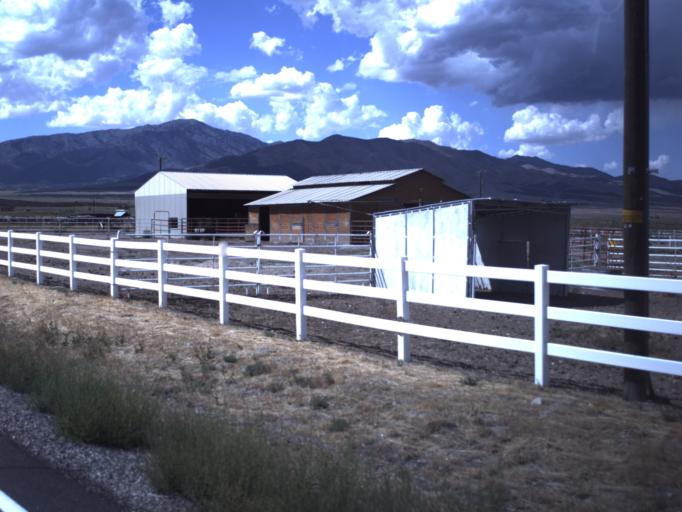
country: US
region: Utah
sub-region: Tooele County
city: Tooele
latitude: 40.3366
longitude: -112.4498
